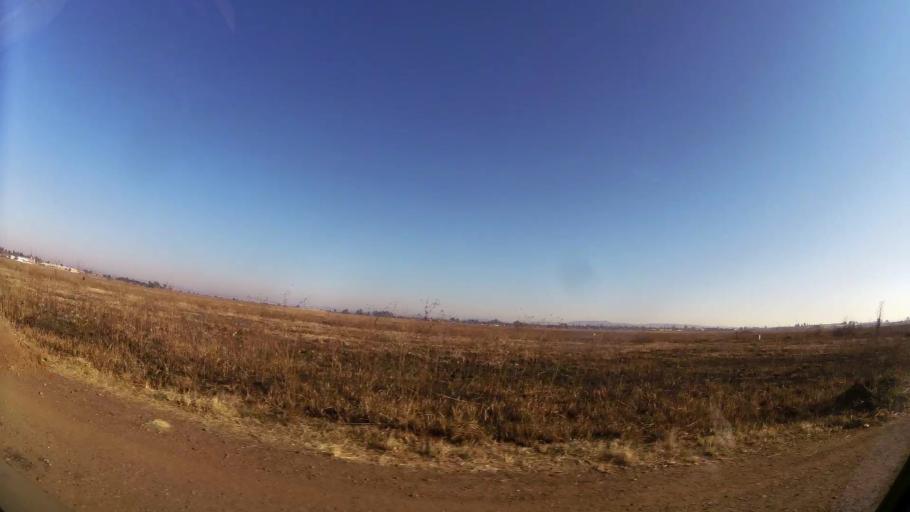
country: ZA
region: Gauteng
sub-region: Ekurhuleni Metropolitan Municipality
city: Germiston
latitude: -26.3394
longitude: 28.1331
